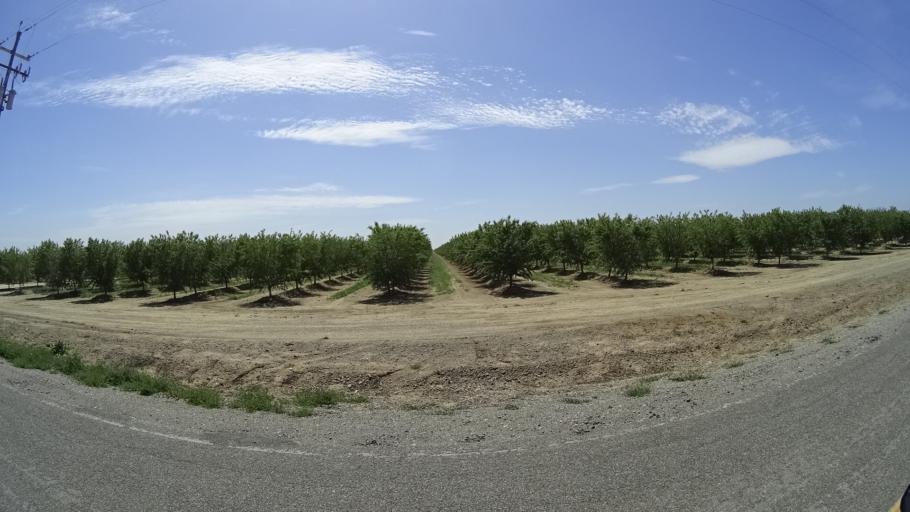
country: US
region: California
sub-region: Glenn County
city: Orland
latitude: 39.6532
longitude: -122.1880
